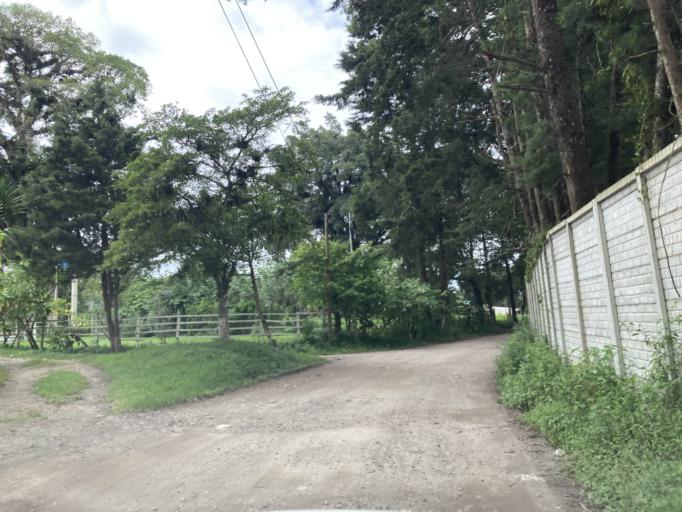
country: GT
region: Guatemala
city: San Jose Pinula
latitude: 14.5322
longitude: -90.4056
